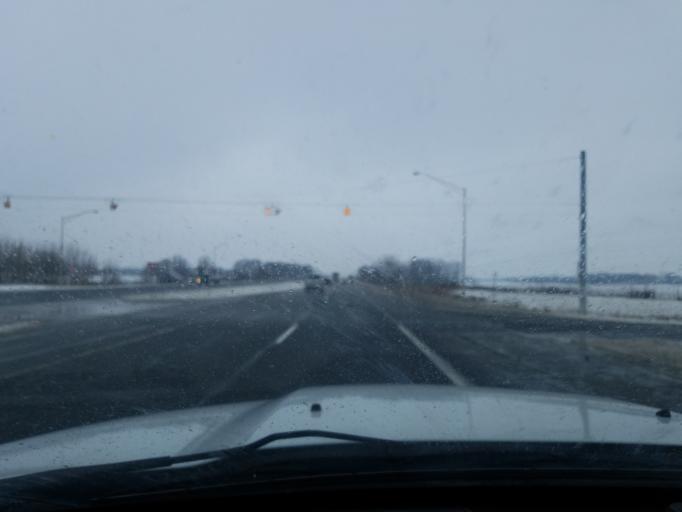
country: US
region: Indiana
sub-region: Marshall County
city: Argos
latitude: 41.1721
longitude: -86.2416
